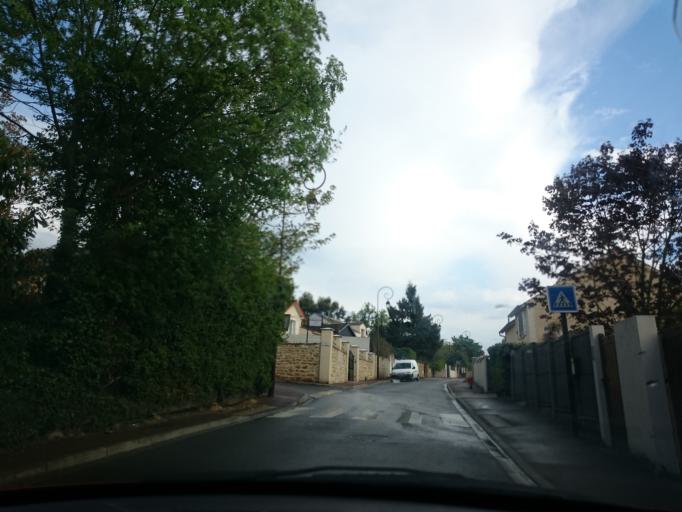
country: FR
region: Ile-de-France
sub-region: Departement de l'Essonne
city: Etiolles
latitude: 48.6324
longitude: 2.4717
